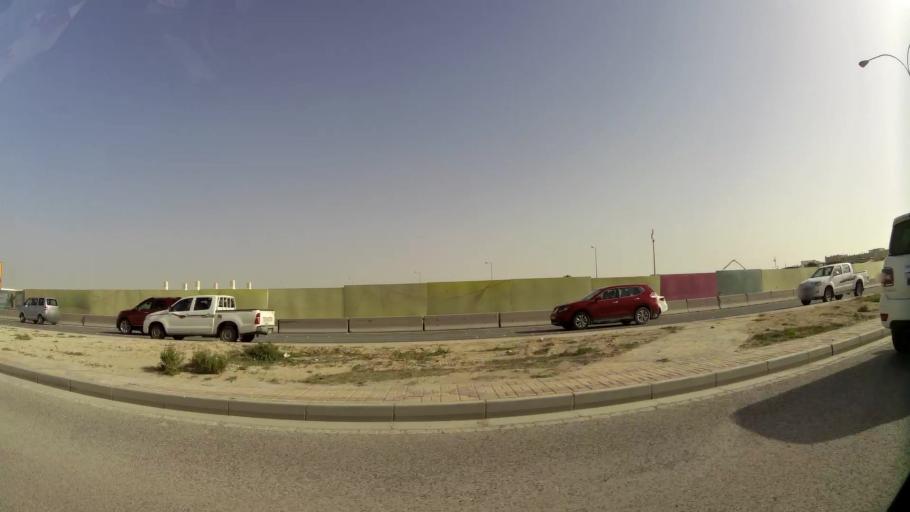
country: QA
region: Baladiyat ar Rayyan
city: Ar Rayyan
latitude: 25.3179
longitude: 51.4311
